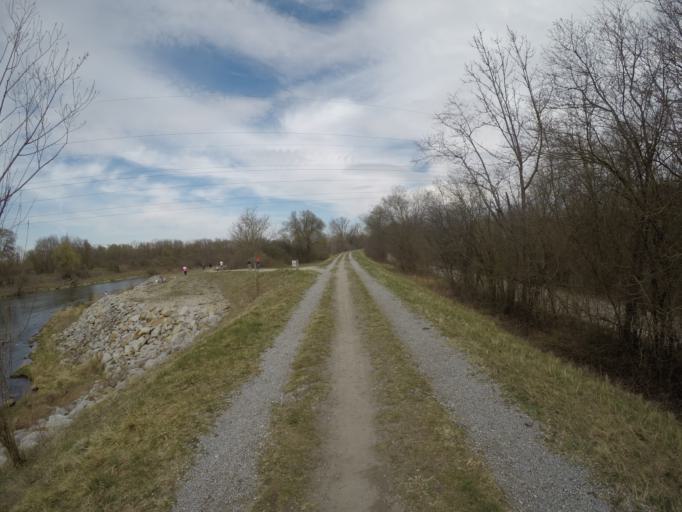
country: DE
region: Bavaria
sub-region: Lower Bavaria
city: Stallwang
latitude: 48.5831
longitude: 12.2234
